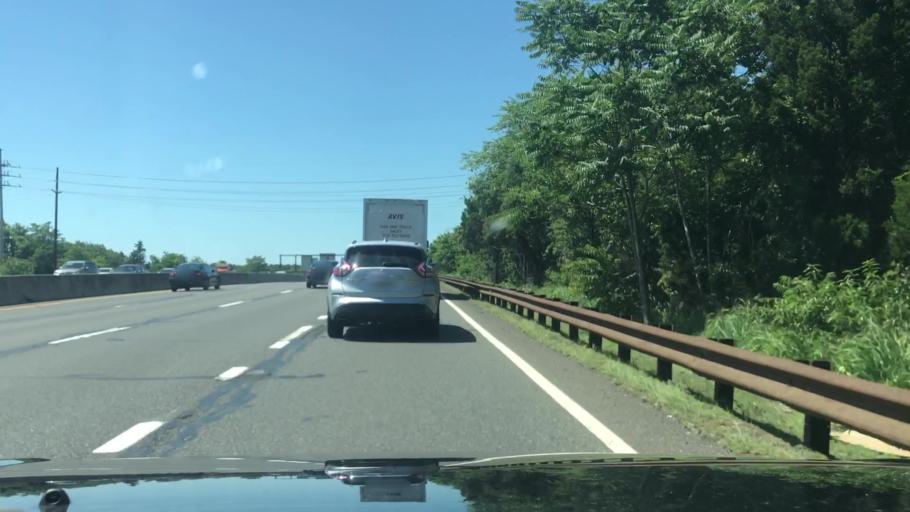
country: US
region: New Jersey
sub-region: Ocean County
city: Toms River
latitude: 39.9532
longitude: -74.2071
